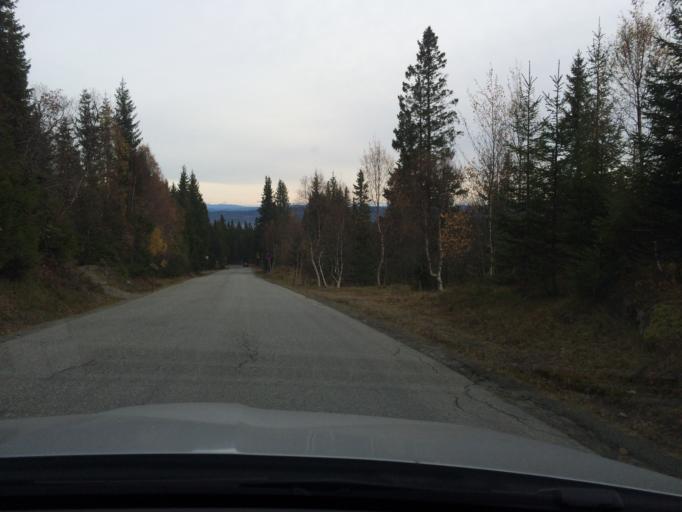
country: NO
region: Sor-Trondelag
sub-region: Trondheim
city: Trondheim
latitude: 63.4153
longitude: 10.2700
